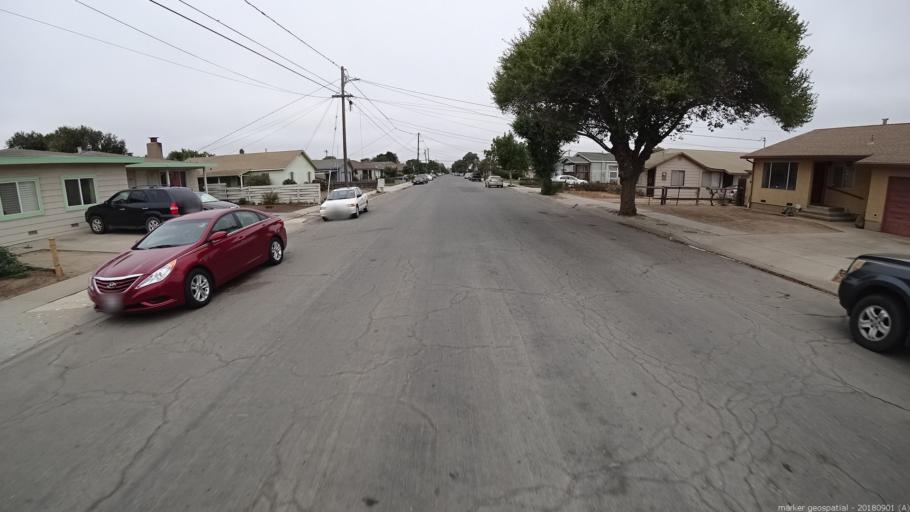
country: US
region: California
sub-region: Monterey County
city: Greenfield
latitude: 36.3186
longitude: -121.2446
